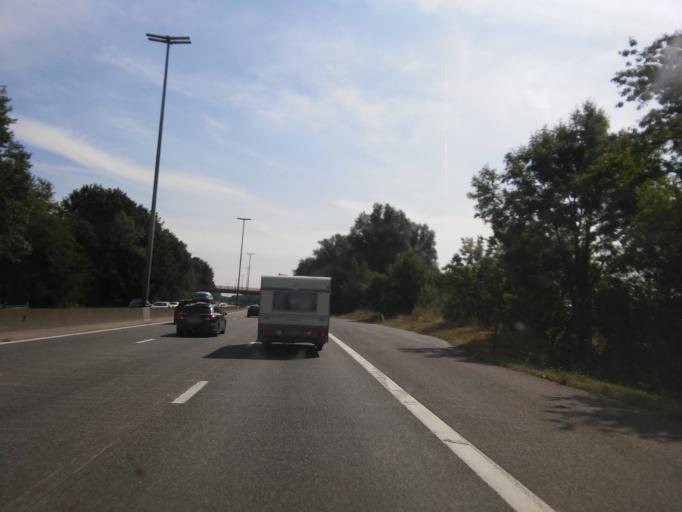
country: BE
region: Flanders
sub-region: Provincie Vlaams-Brabant
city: Ternat
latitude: 50.8807
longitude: 4.1796
